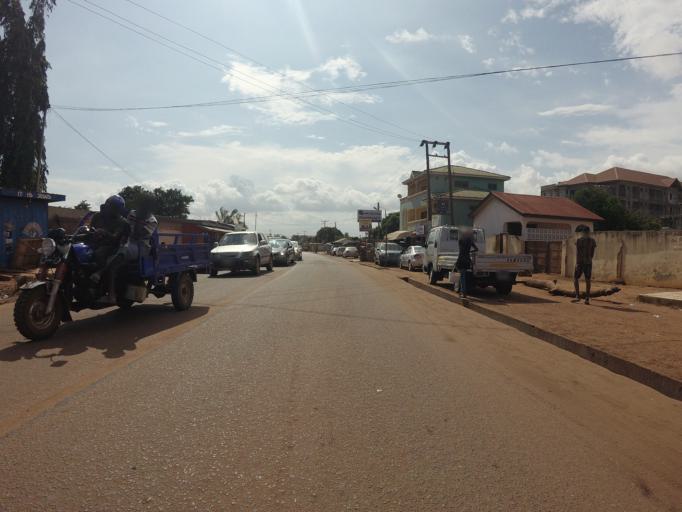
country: GH
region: Greater Accra
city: Medina Estates
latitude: 5.6786
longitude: -0.1747
